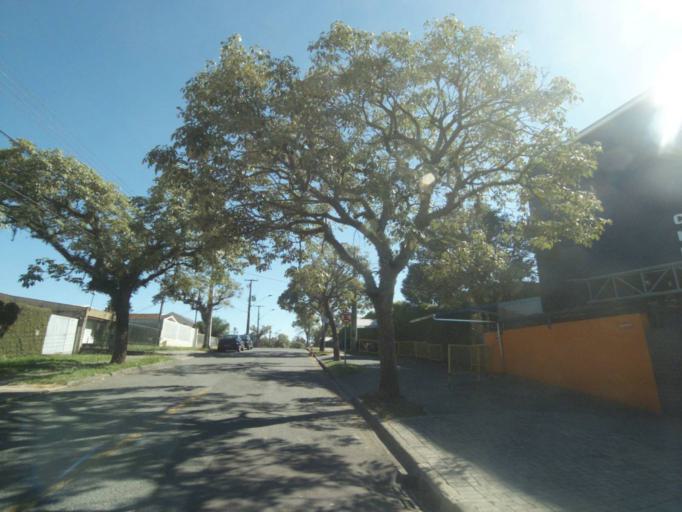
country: BR
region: Parana
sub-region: Curitiba
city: Curitiba
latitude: -25.3910
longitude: -49.2340
